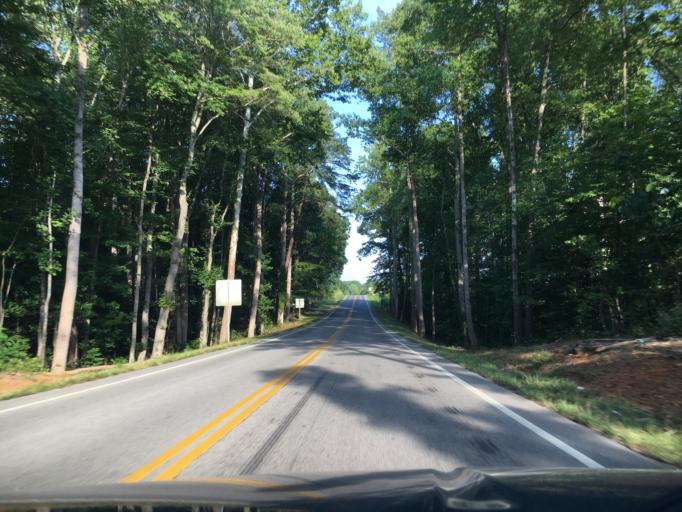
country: US
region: Virginia
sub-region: Franklin County
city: Union Hall
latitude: 36.9754
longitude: -79.6136
